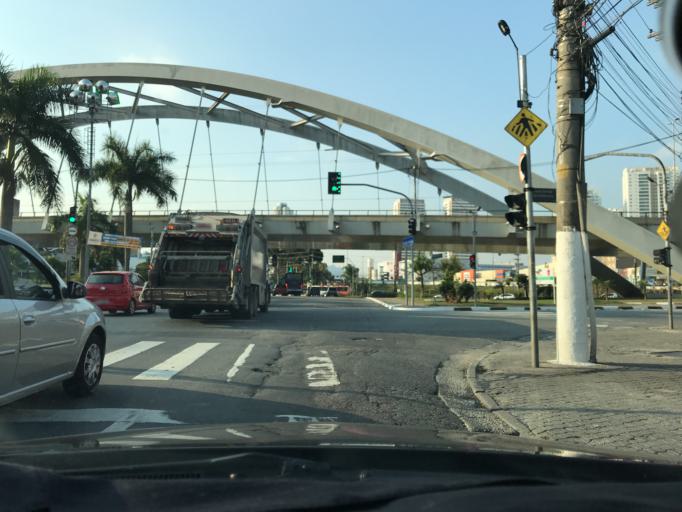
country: BR
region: Sao Paulo
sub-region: Osasco
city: Osasco
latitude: -23.5399
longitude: -46.7725
